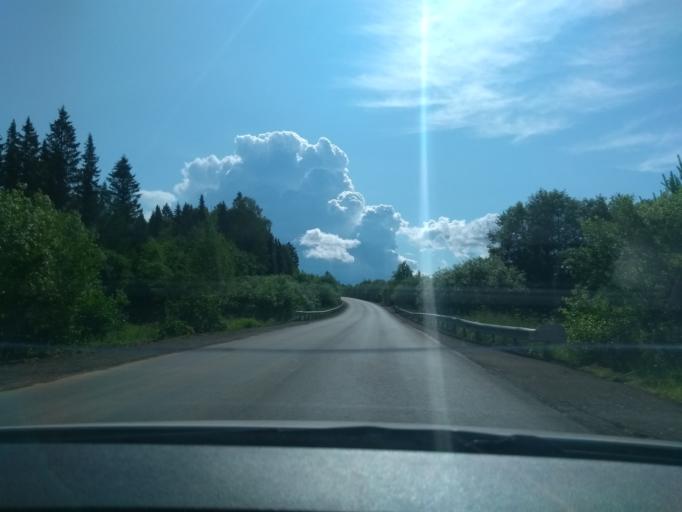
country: RU
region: Perm
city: Kukushtan
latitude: 57.8161
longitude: 56.5425
